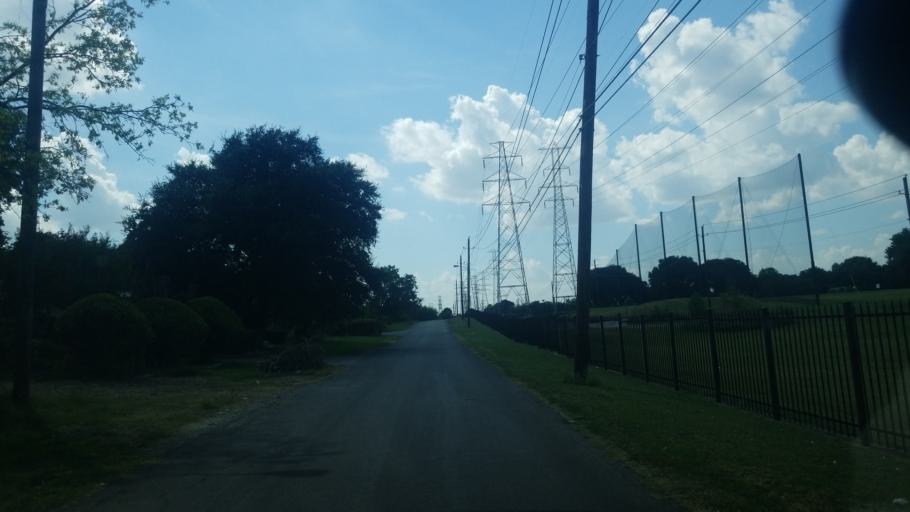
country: US
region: Texas
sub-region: Dallas County
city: Dallas
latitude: 32.7200
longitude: -96.7970
